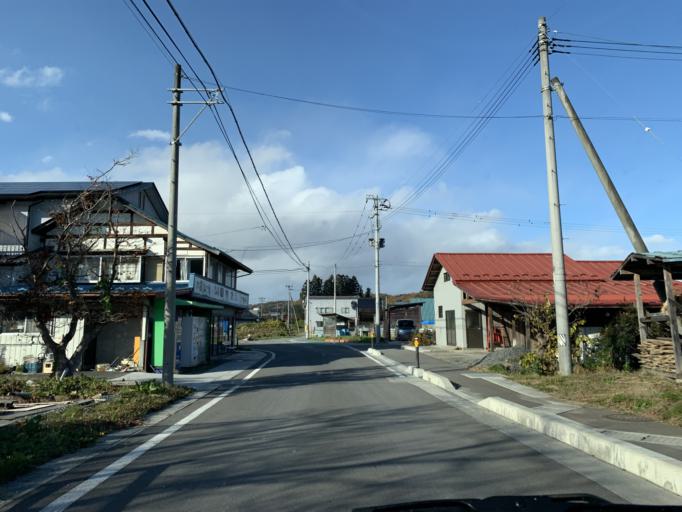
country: JP
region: Iwate
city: Ichinoseki
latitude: 39.0074
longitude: 141.1001
